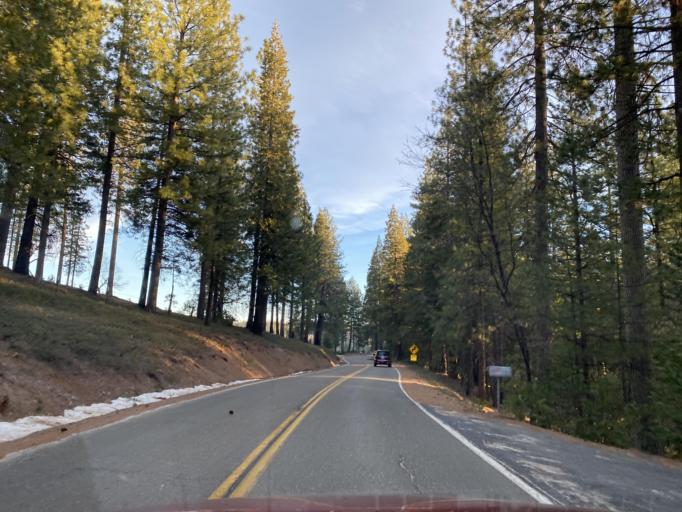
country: US
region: California
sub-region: Amador County
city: Pioneer
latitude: 38.5043
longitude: -120.5207
